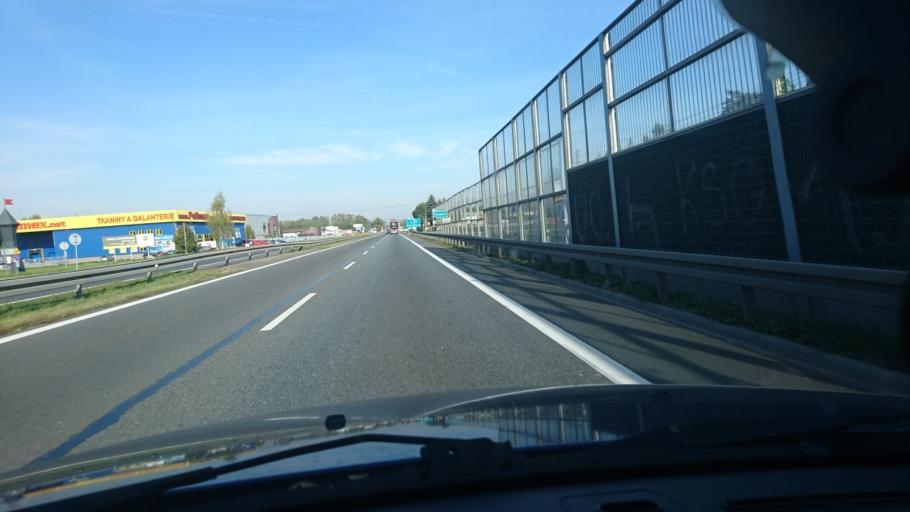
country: PL
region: Silesian Voivodeship
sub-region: Powiat pszczynski
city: Goczalkowice Zdroj
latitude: 49.9604
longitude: 18.9619
